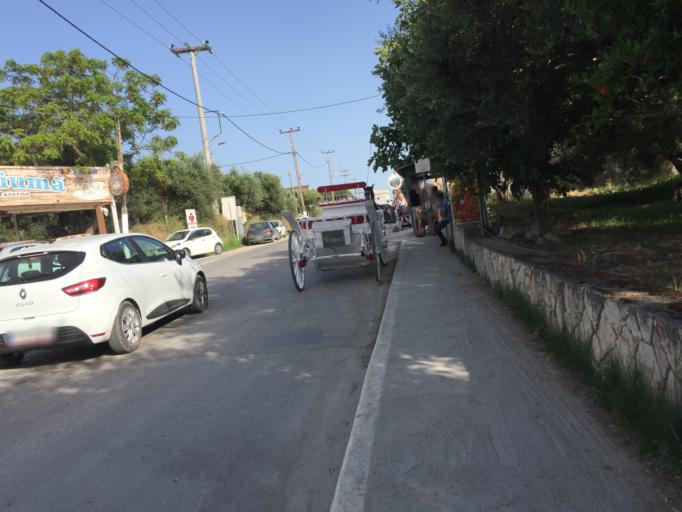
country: GR
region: Ionian Islands
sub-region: Nomos Zakynthou
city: Vanaton
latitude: 37.8180
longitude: 20.8625
